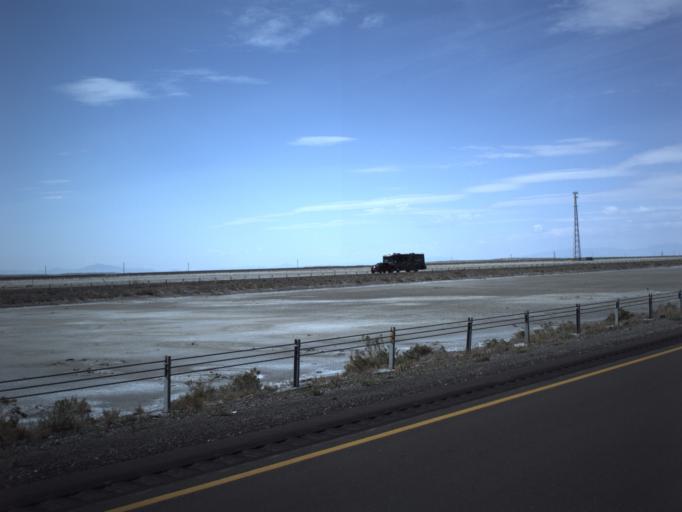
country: US
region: Utah
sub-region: Tooele County
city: Wendover
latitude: 40.7283
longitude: -113.3209
